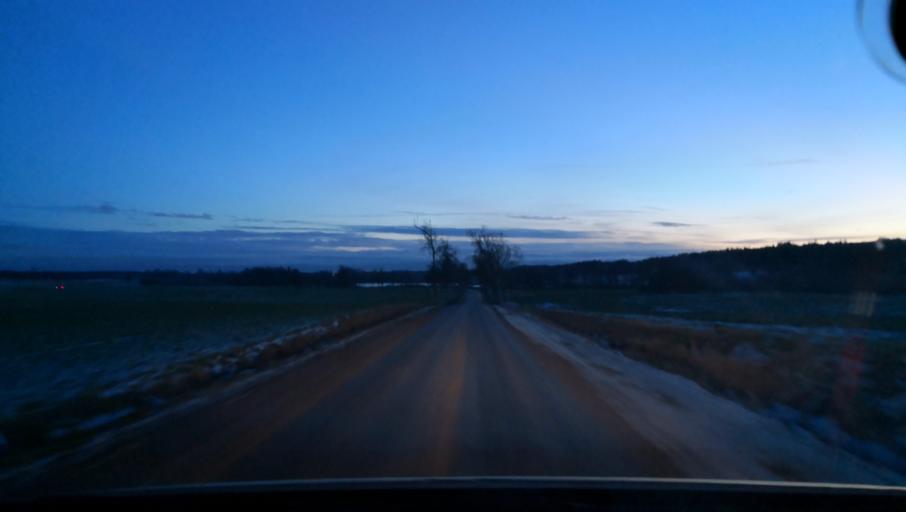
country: SE
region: Soedermanland
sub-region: Katrineholms Kommun
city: Katrineholm
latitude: 59.0826
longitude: 16.3189
